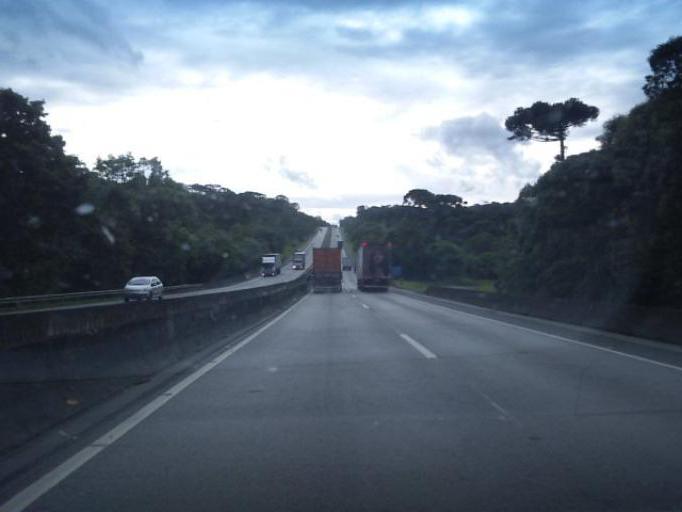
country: BR
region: Parana
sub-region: Campina Grande Do Sul
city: Campina Grande do Sul
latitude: -25.3041
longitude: -48.9684
